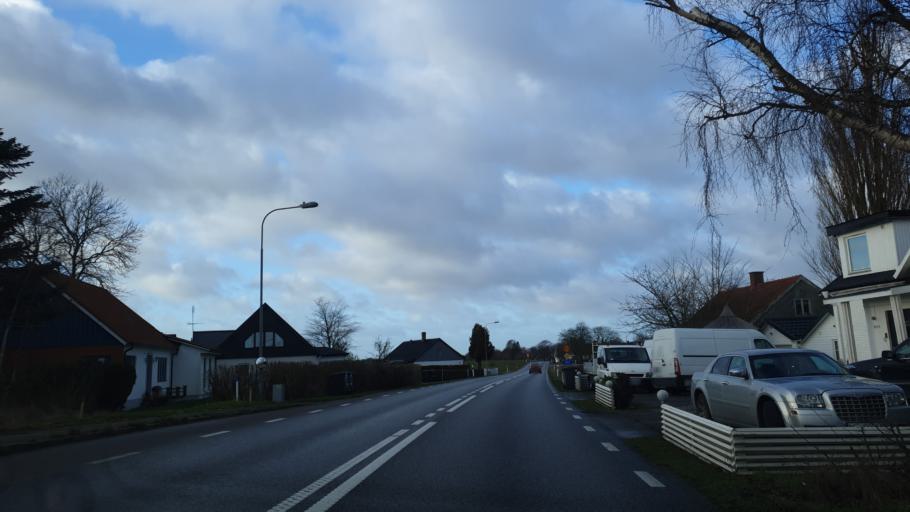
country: SE
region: Skane
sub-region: Trelleborgs Kommun
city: Trelleborg
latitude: 55.4608
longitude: 13.1528
